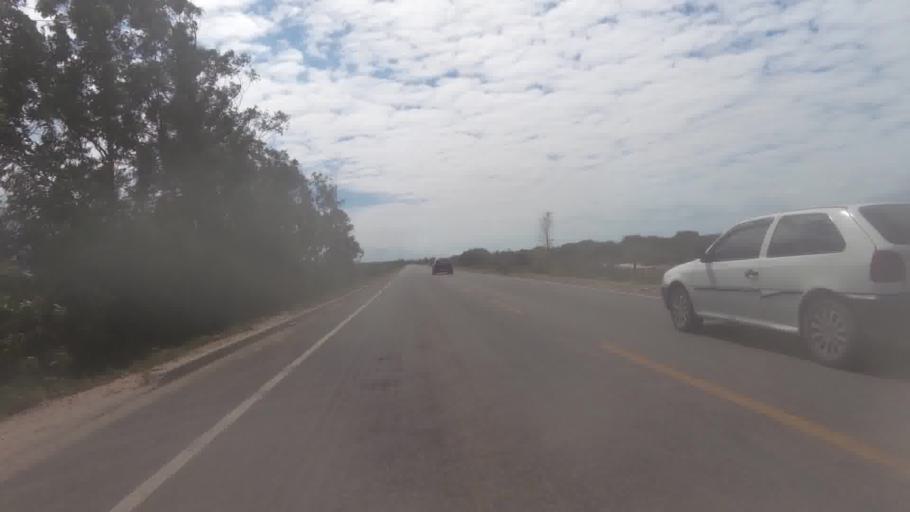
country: BR
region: Espirito Santo
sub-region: Marataizes
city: Marataizes
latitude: -21.2238
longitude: -40.9714
